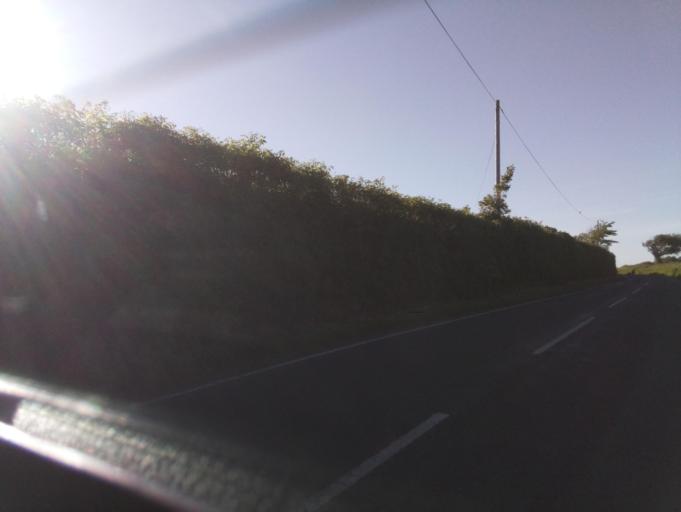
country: GB
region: England
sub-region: Dorset
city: Lyme Regis
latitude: 50.7194
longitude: -2.9892
